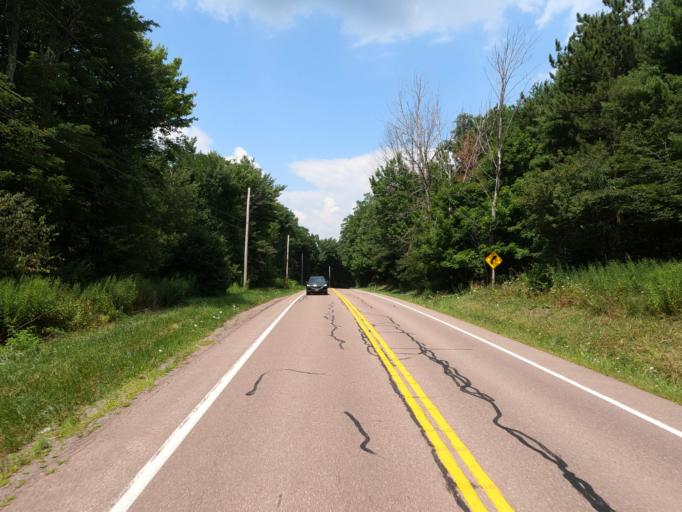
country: US
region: Maryland
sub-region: Allegany County
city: Westernport
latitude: 39.6462
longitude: -79.1986
